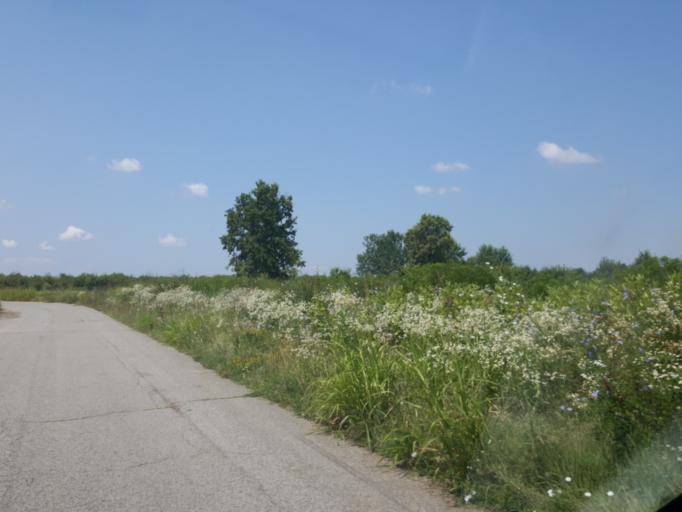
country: RS
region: Autonomna Pokrajina Vojvodina
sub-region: Sremski Okrug
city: Sid
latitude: 45.0480
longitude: 19.1762
